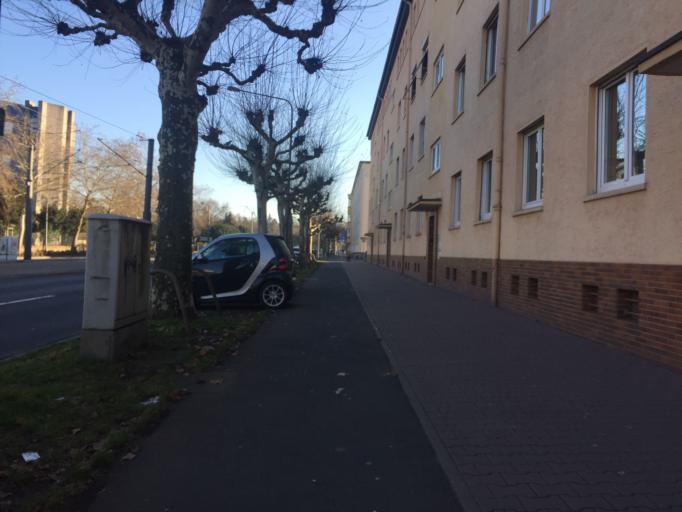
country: DE
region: Hesse
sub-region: Regierungsbezirk Darmstadt
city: Frankfurt am Main
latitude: 50.1417
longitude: 8.6835
